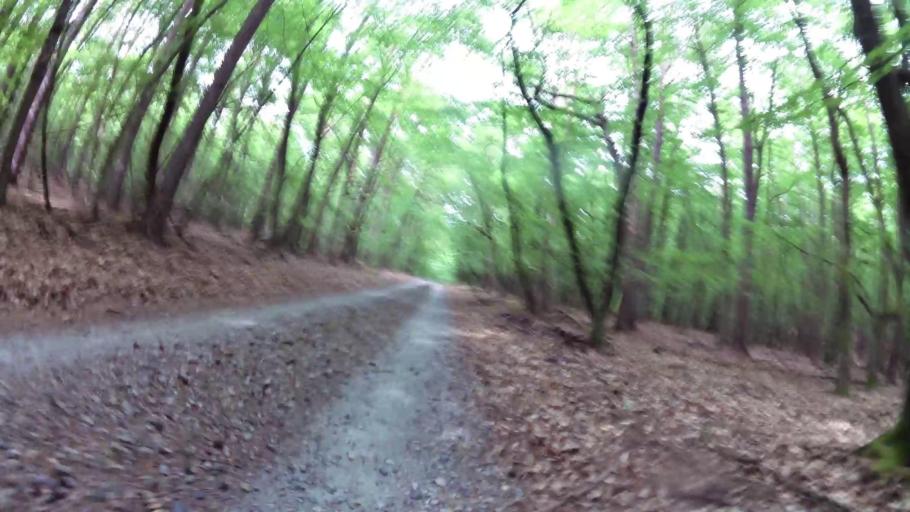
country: PL
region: West Pomeranian Voivodeship
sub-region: Powiat kamienski
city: Miedzyzdroje
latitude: 53.9397
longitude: 14.4968
